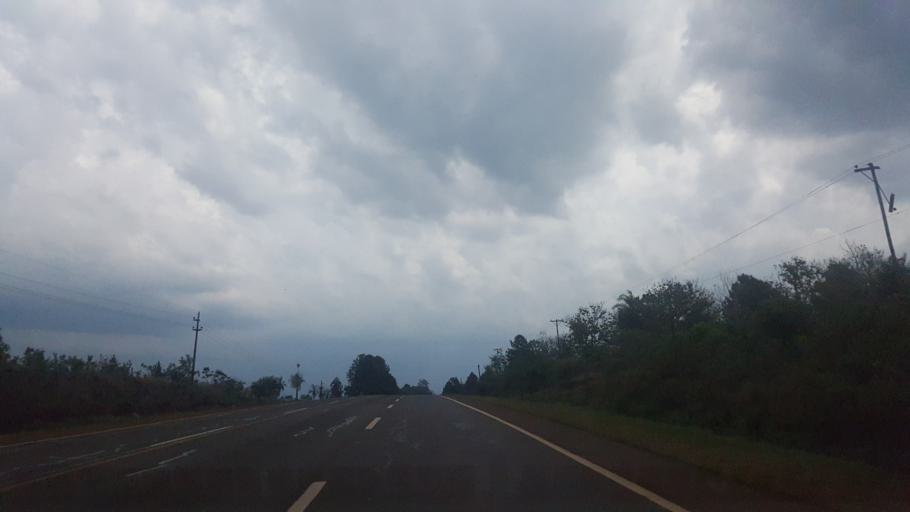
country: AR
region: Misiones
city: Santo Pipo
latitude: -27.1254
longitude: -55.3827
